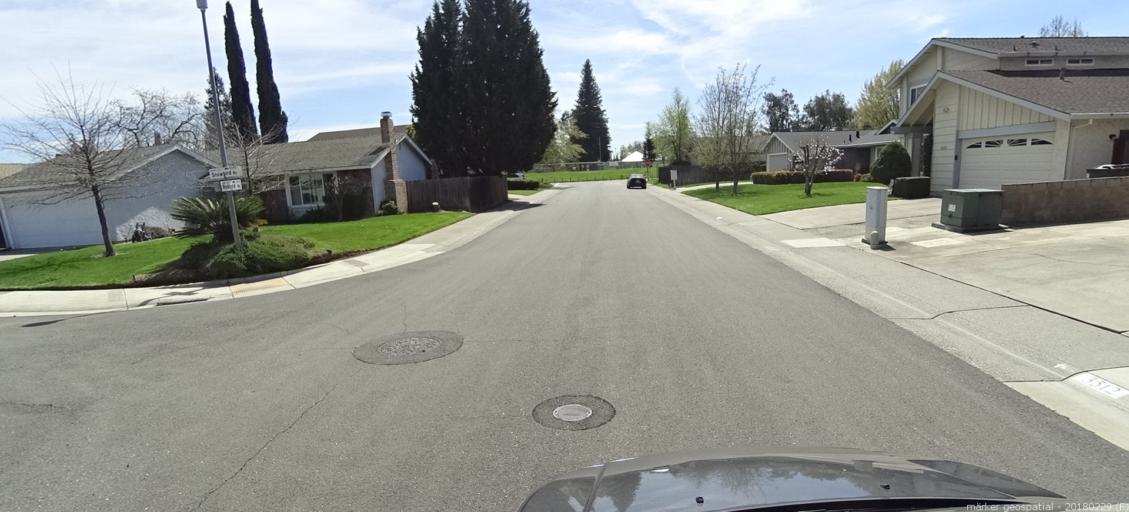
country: US
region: California
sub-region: Sacramento County
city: Rosemont
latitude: 38.5533
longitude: -121.3518
